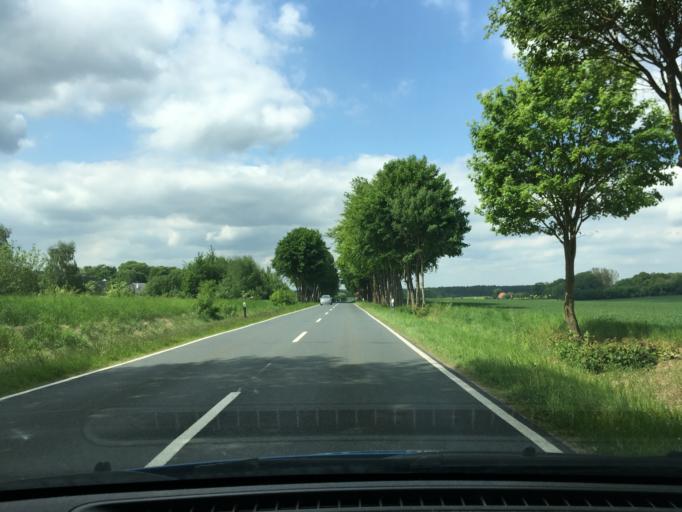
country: DE
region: Lower Saxony
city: Wendisch Evern
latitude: 53.2206
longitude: 10.4691
